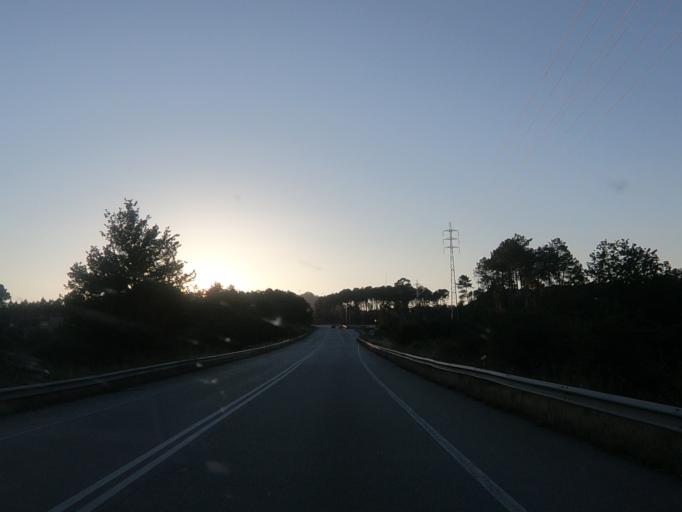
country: PT
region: Viseu
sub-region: Viseu
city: Abraveses
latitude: 40.6882
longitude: -7.9013
